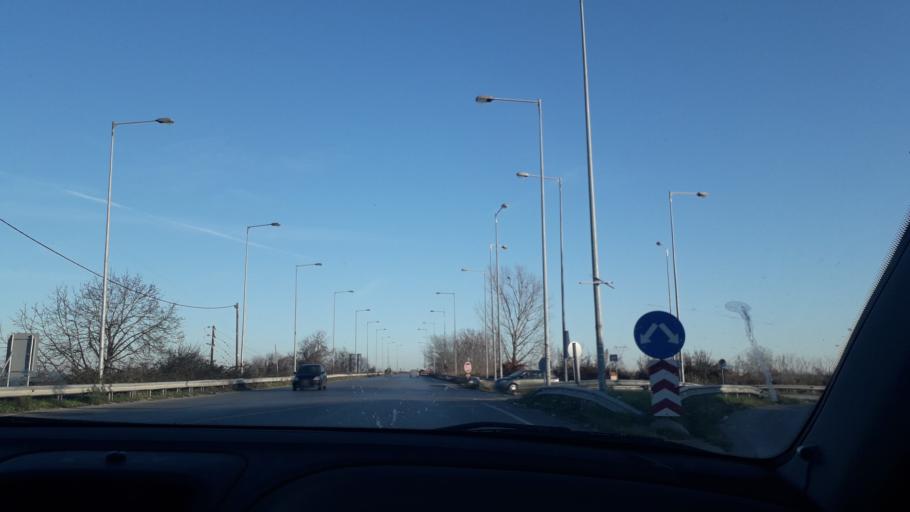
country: GR
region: Central Macedonia
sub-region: Nomos Imathias
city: Agkathia
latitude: 40.5910
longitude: 22.4672
